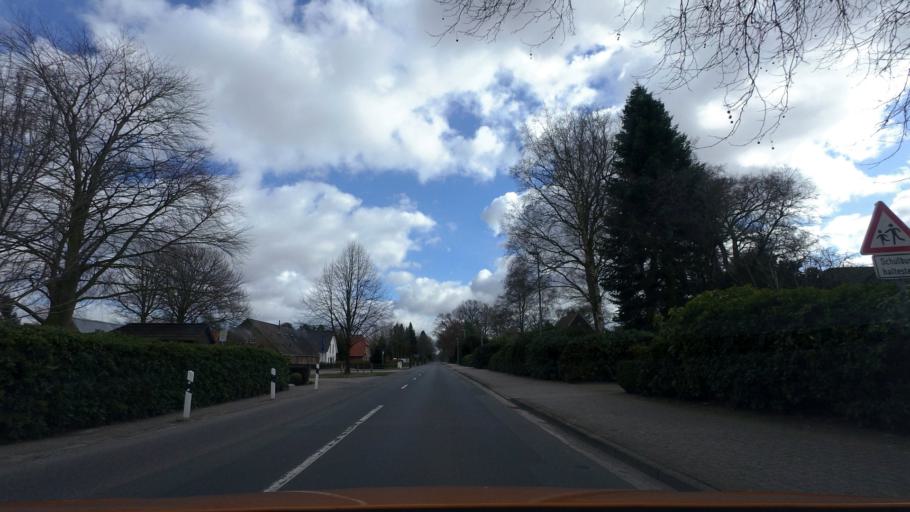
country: DE
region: Lower Saxony
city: Bad Zwischenahn
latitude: 53.1498
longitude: 8.0842
